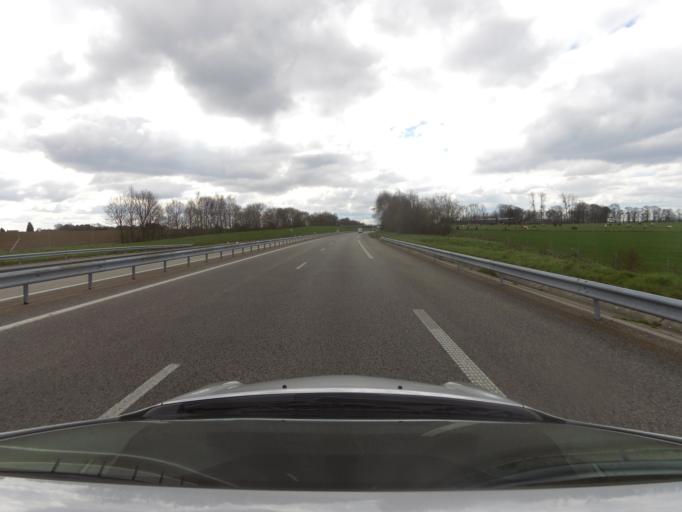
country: FR
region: Haute-Normandie
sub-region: Departement de la Seine-Maritime
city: Saint-Aubin-Routot
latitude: 49.5270
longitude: 0.3098
